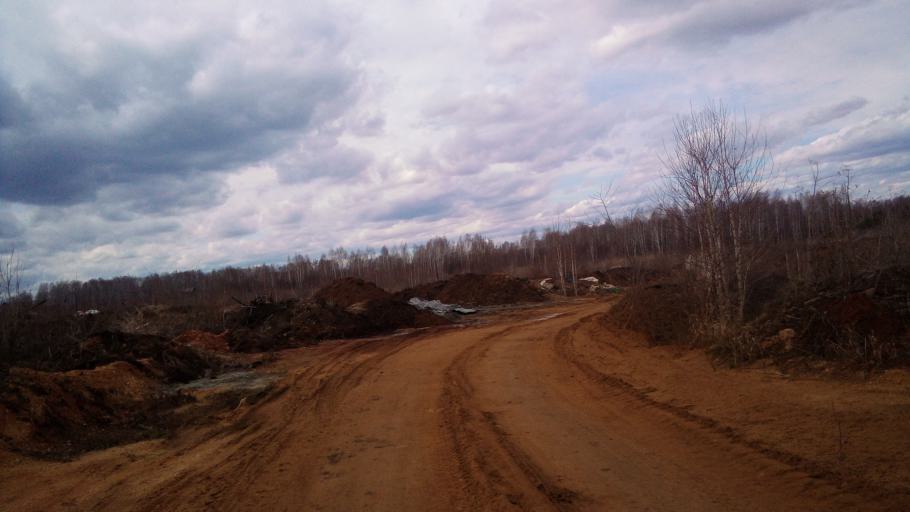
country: RU
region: Chelyabinsk
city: Sargazy
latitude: 55.1255
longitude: 61.2580
